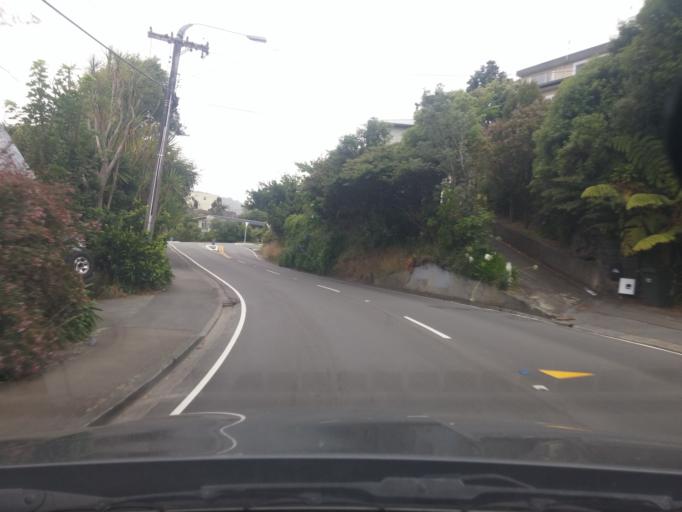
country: NZ
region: Wellington
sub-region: Wellington City
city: Kelburn
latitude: -41.2679
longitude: 174.7613
